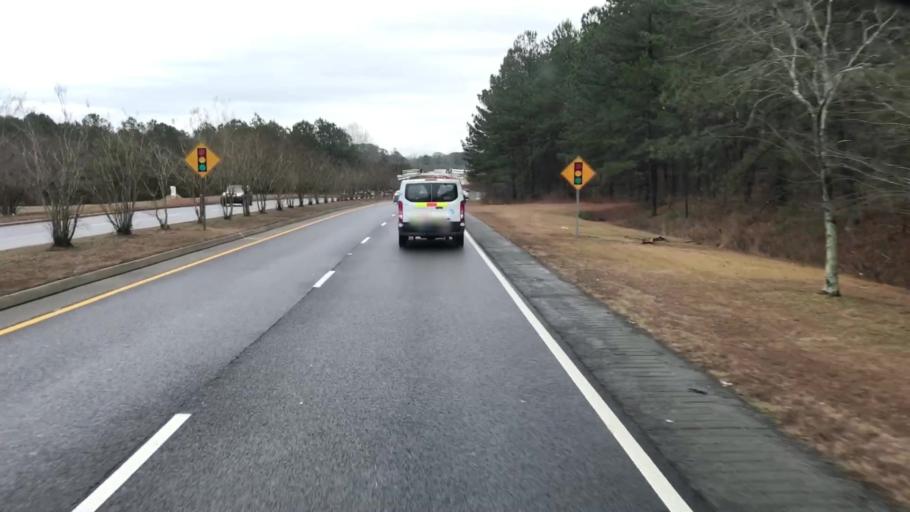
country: US
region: Georgia
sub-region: Gwinnett County
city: Snellville
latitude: 33.8749
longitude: -84.0209
